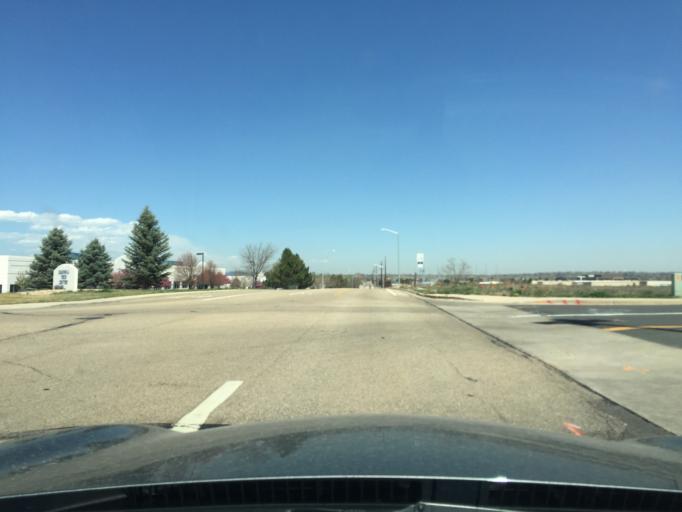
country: US
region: Colorado
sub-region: Boulder County
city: Niwot
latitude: 40.1378
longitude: -105.1404
